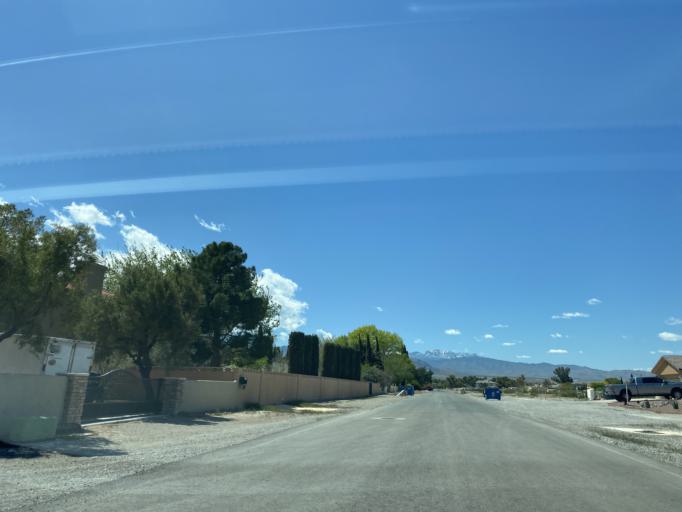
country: US
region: Nevada
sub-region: Clark County
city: North Las Vegas
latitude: 36.2997
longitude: -115.2423
